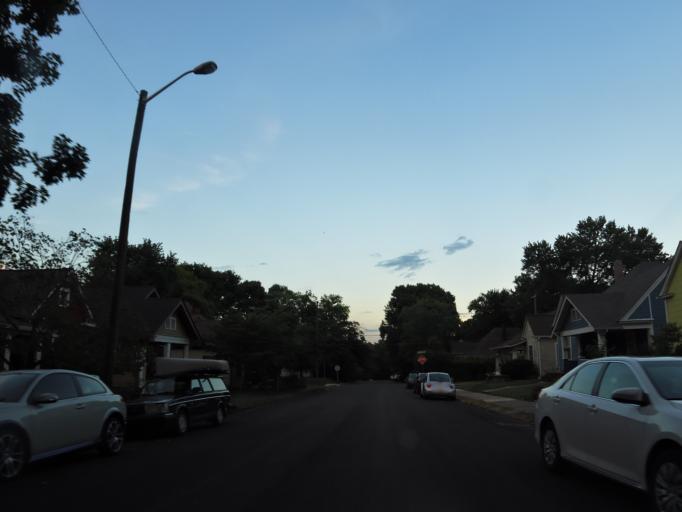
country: US
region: Tennessee
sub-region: Knox County
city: Knoxville
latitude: 35.9875
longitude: -83.9195
